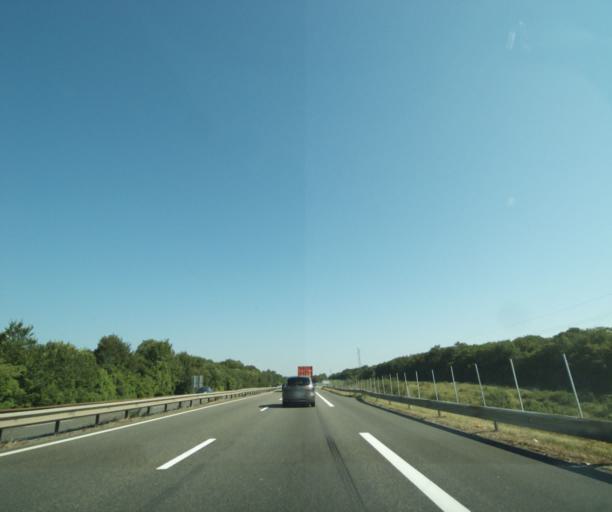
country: FR
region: Lorraine
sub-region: Departement de Meurthe-et-Moselle
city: Laxou
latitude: 48.6810
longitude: 6.1191
